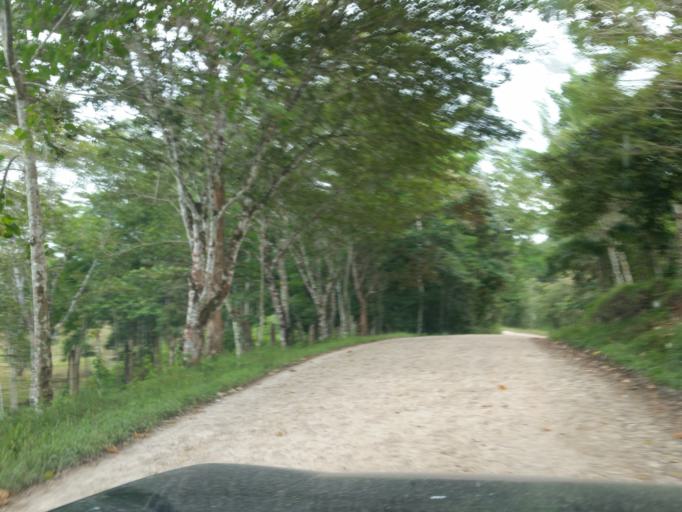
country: CR
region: Alajuela
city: Los Chiles
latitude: 11.1178
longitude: -84.5987
